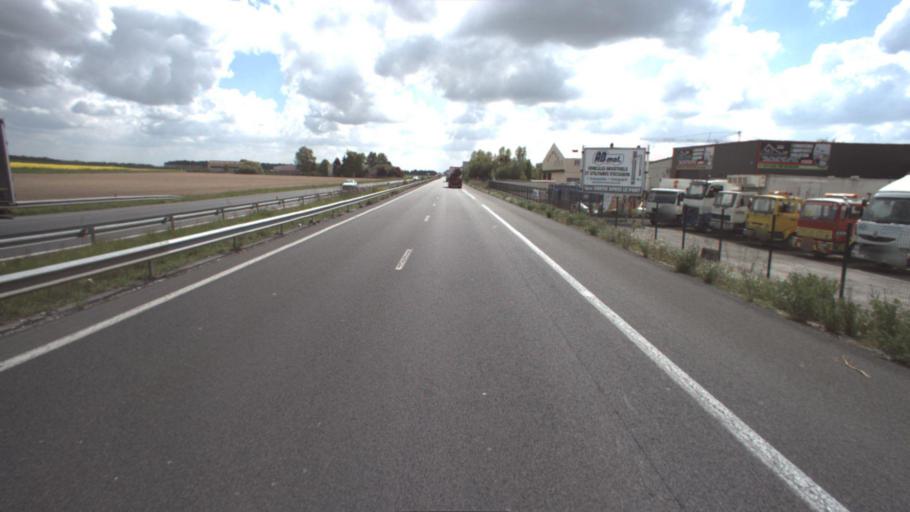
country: FR
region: Ile-de-France
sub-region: Departement de Seine-et-Marne
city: Fontenay-Tresigny
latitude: 48.7023
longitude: 2.8867
